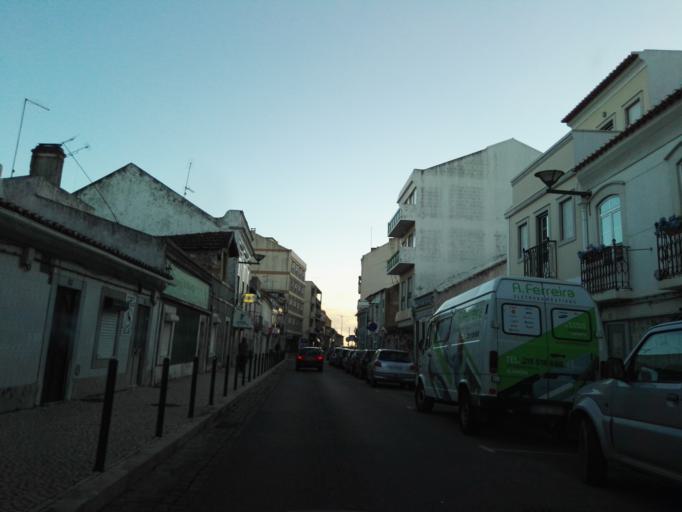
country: PT
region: Lisbon
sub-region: Vila Franca de Xira
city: Vila Franca de Xira
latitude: 38.9528
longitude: -8.9898
